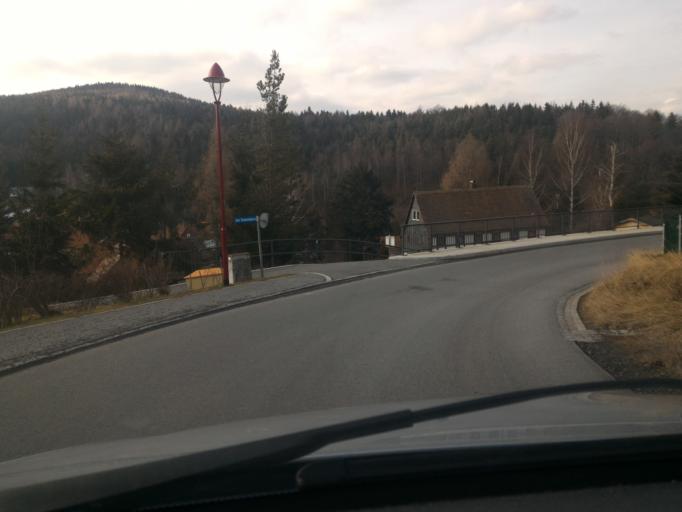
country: DE
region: Saxony
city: Kurort Jonsdorf
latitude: 50.8550
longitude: 14.6951
